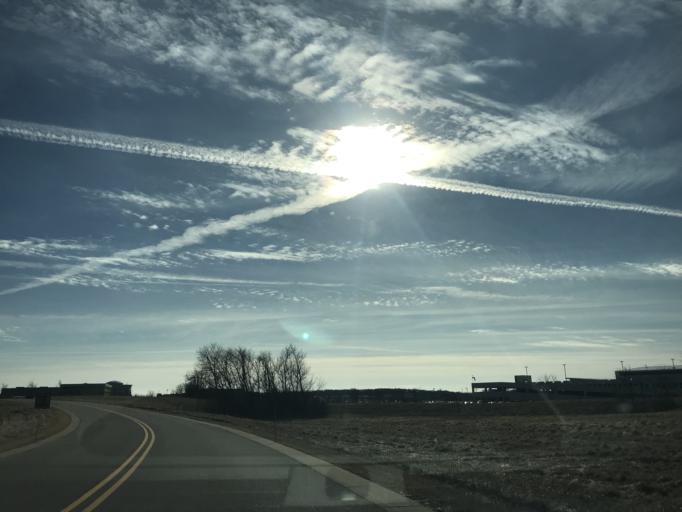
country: US
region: Wisconsin
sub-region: Dane County
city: Windsor
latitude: 43.1570
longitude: -89.2973
